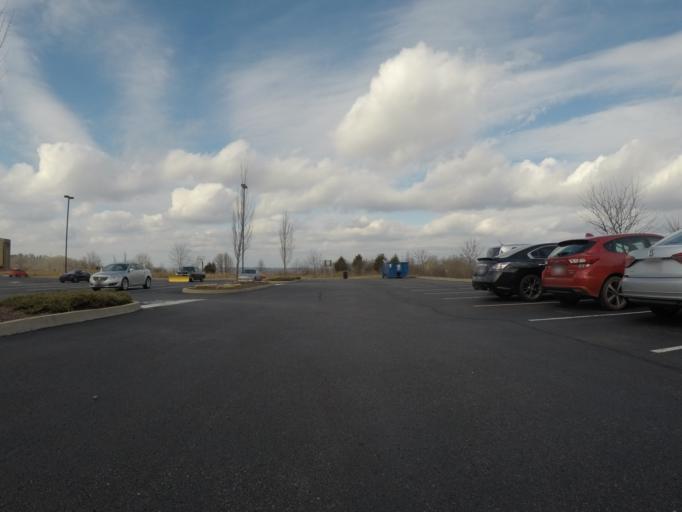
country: US
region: West Virginia
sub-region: Cabell County
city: Huntington
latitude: 38.3949
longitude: -82.4202
